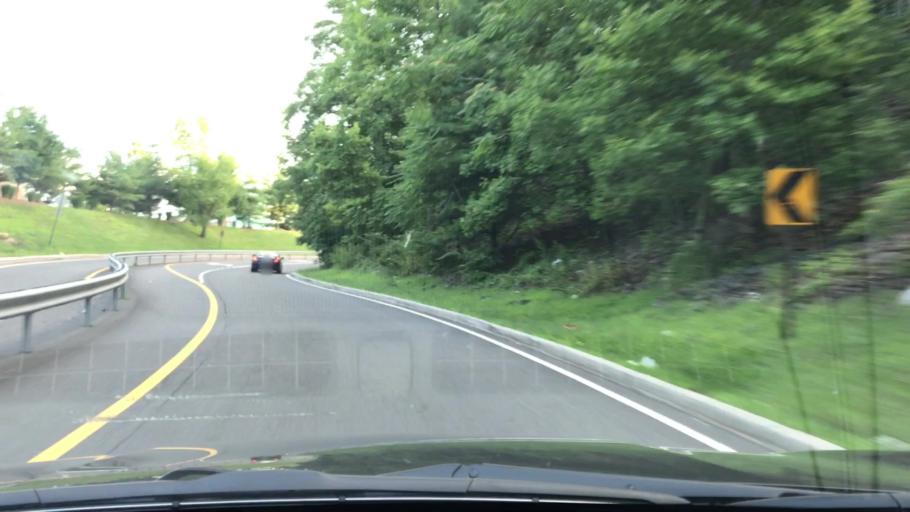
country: US
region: New York
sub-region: Westchester County
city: Hastings-on-Hudson
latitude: 40.9734
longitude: -73.8782
